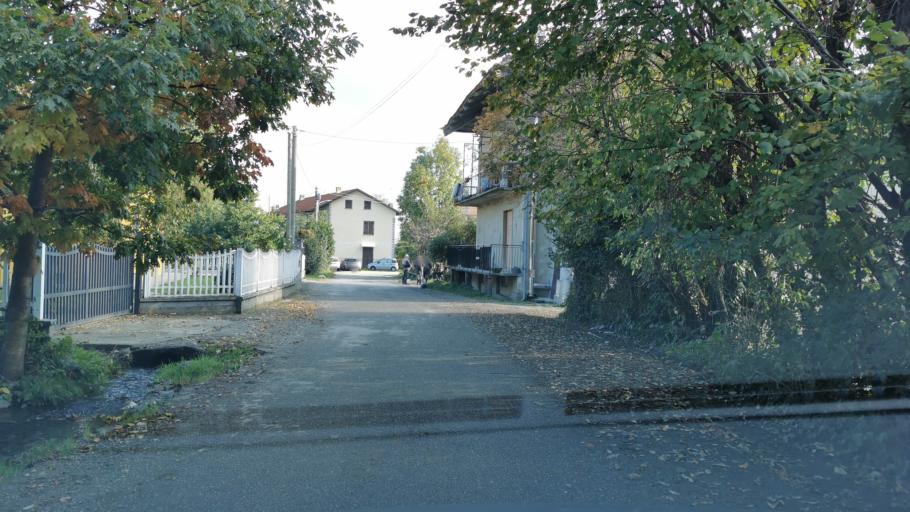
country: IT
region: Piedmont
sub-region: Provincia di Torino
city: Cafasse
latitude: 45.2473
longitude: 7.5200
